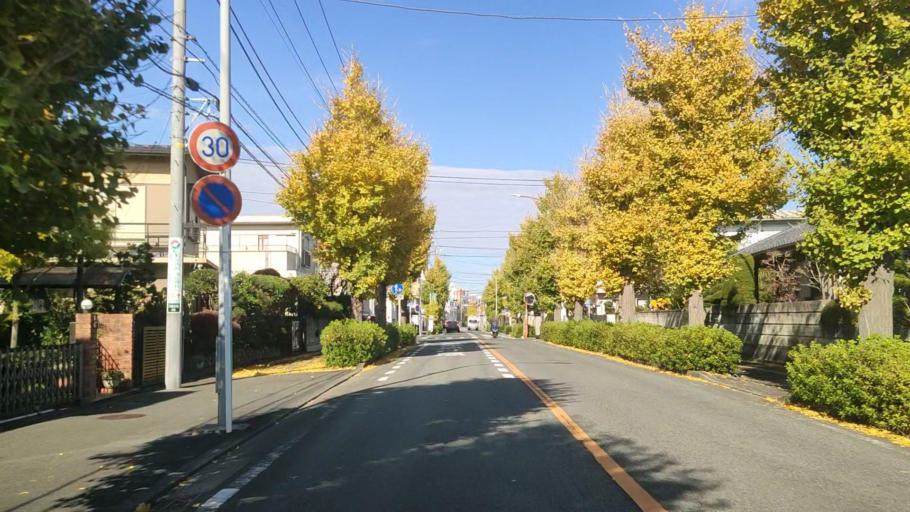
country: JP
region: Kanagawa
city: Minami-rinkan
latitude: 35.4561
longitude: 139.5345
